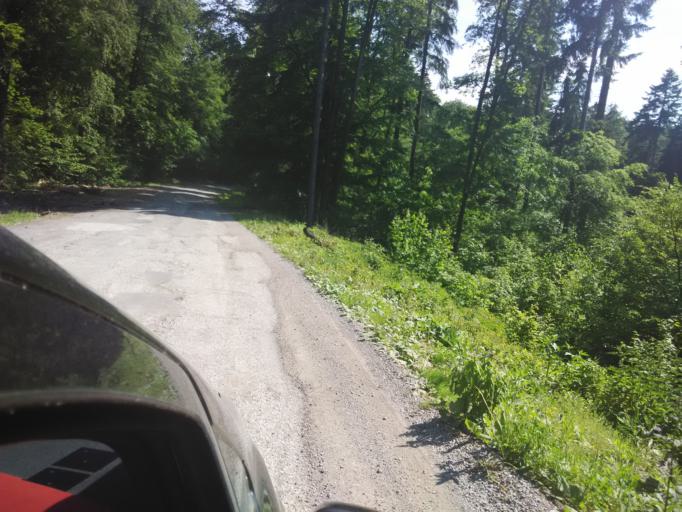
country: SK
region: Banskobystricky
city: Revuca
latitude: 48.6505
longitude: 20.2962
